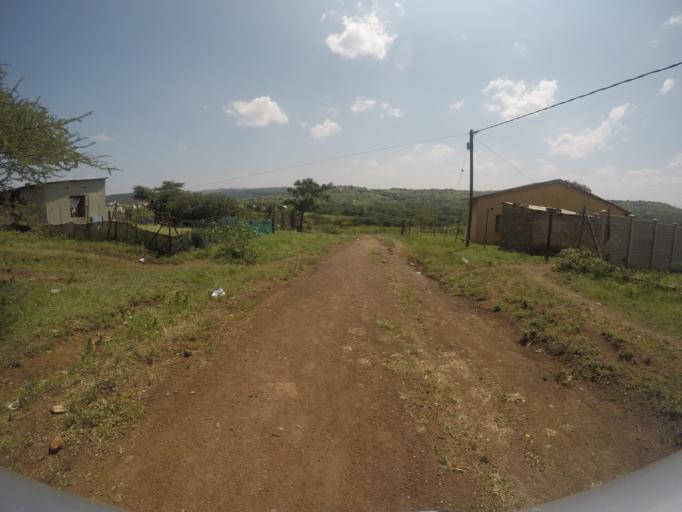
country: ZA
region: KwaZulu-Natal
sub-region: uThungulu District Municipality
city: Empangeni
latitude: -28.5928
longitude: 31.7371
